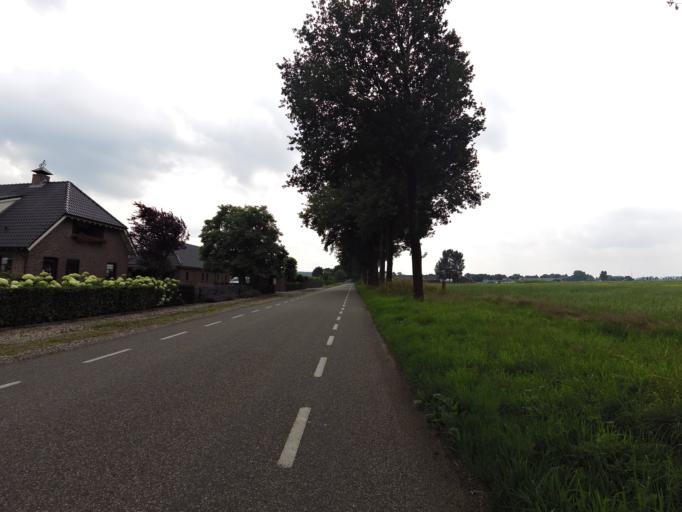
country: NL
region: Gelderland
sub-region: Gemeente Montferland
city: s-Heerenberg
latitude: 51.9361
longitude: 6.2032
